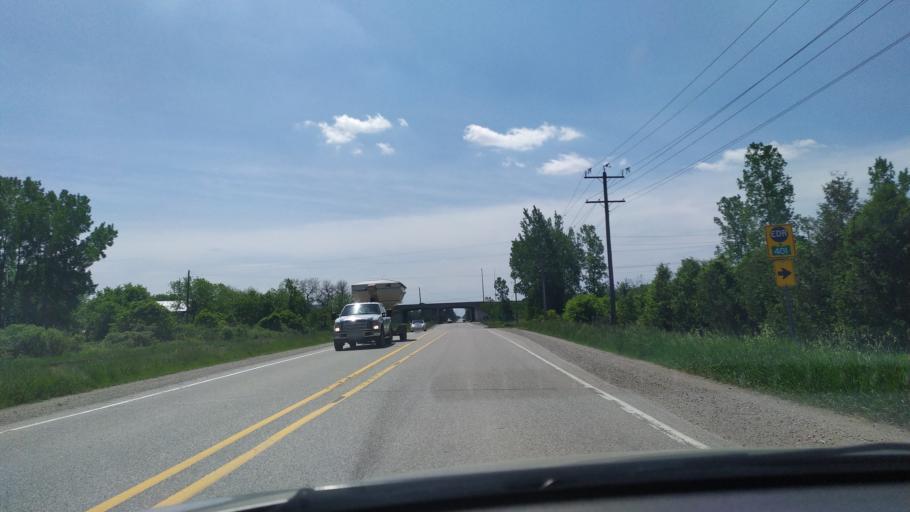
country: CA
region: Ontario
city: Ingersoll
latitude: 42.9790
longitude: -80.9513
